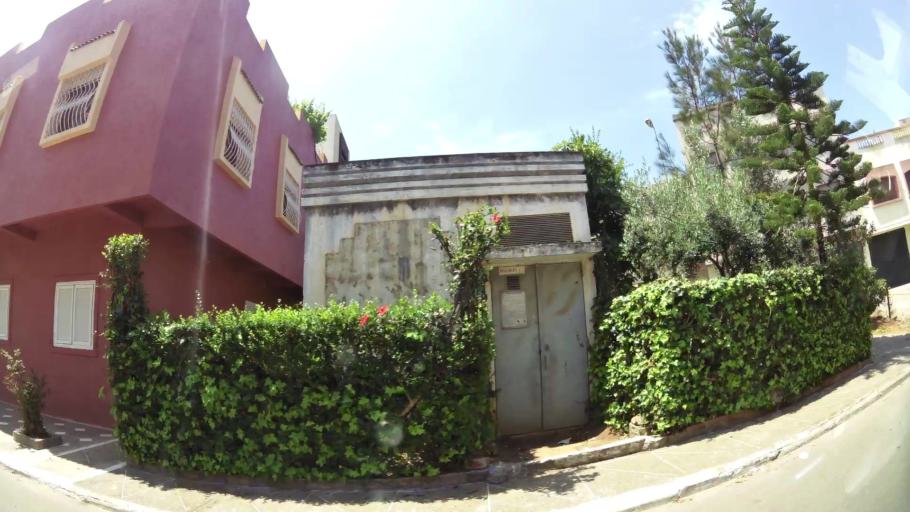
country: MA
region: Gharb-Chrarda-Beni Hssen
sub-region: Kenitra Province
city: Kenitra
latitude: 34.2723
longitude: -6.6110
